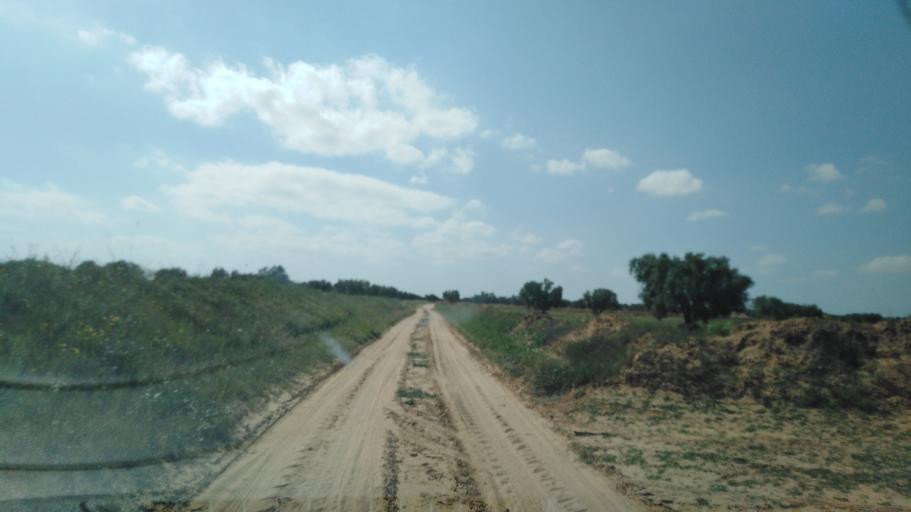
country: TN
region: Safaqis
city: Bi'r `Ali Bin Khalifah
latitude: 34.7916
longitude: 10.4020
